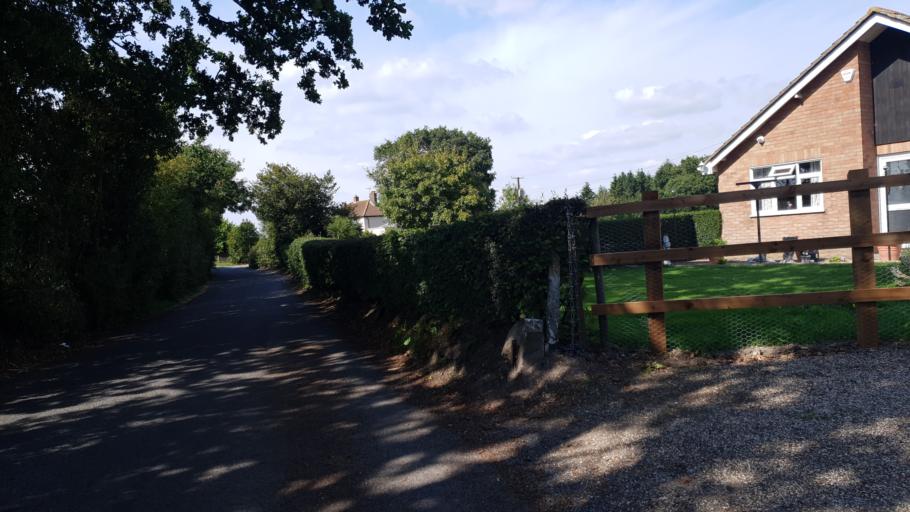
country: GB
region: England
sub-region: Essex
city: Colchester
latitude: 51.9272
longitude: 0.9629
